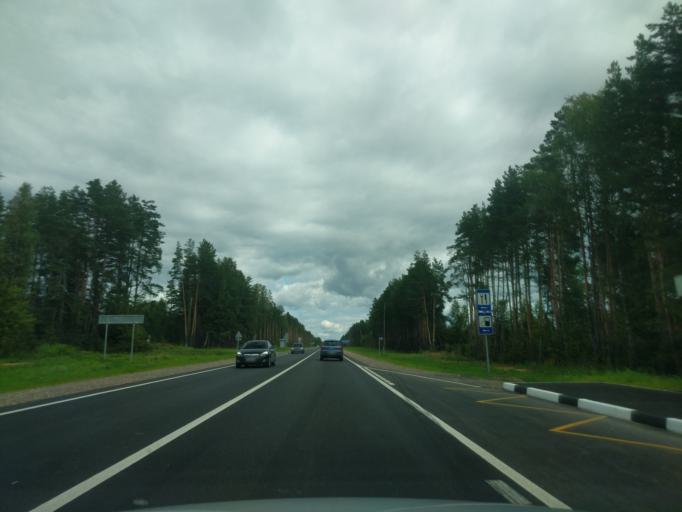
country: RU
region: Jaroslavl
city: Nekrasovskoye
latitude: 57.5784
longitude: 40.2801
